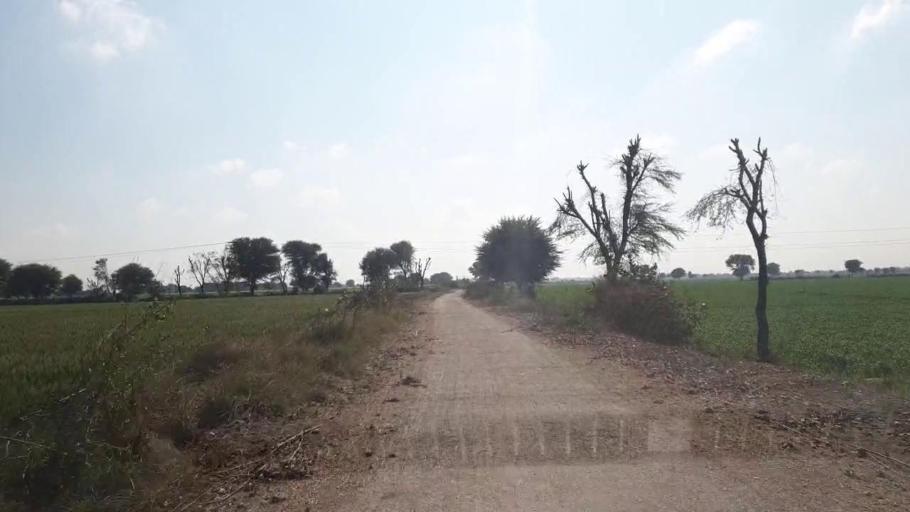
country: PK
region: Sindh
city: Shahpur Chakar
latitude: 26.0526
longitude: 68.5993
